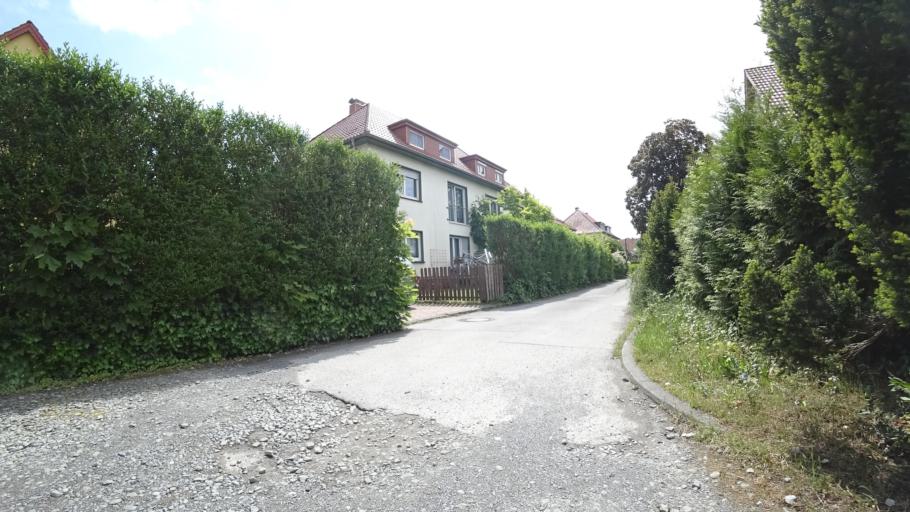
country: DE
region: North Rhine-Westphalia
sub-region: Regierungsbezirk Detmold
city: Guetersloh
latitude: 51.9061
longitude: 8.3975
